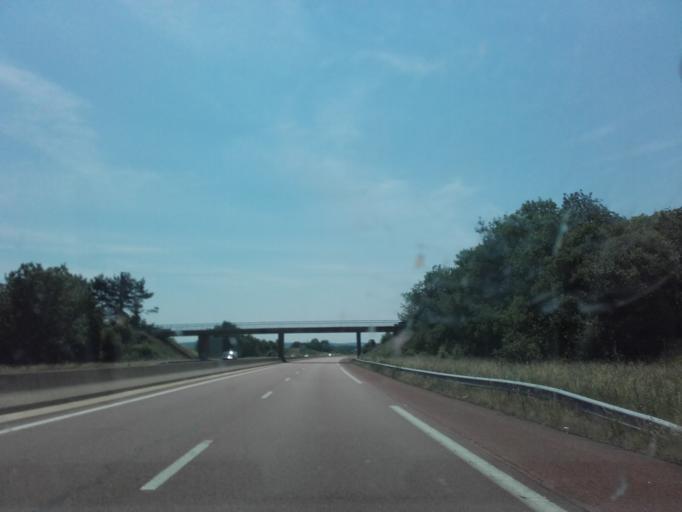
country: FR
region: Bourgogne
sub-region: Departement de la Cote-d'Or
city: Pouilly-en-Auxois
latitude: 47.2423
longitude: 4.5771
